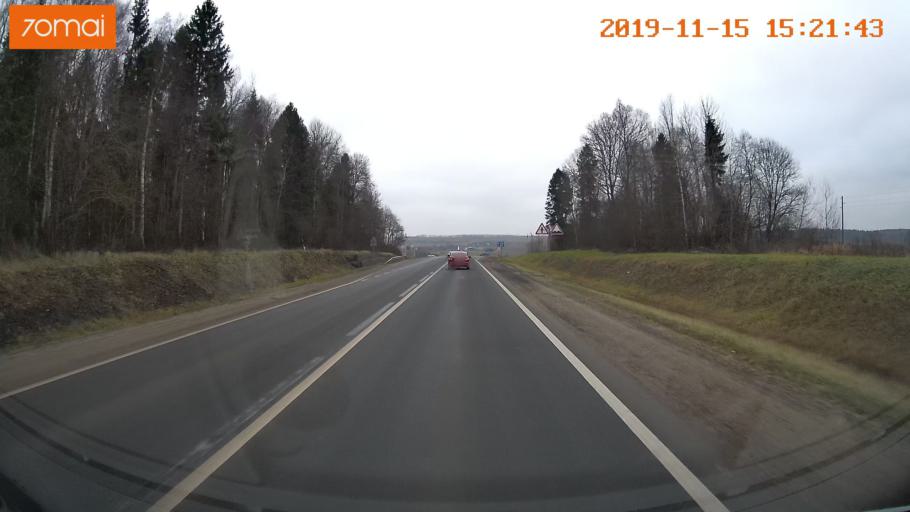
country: RU
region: Jaroslavl
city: Danilov
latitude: 58.2097
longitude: 40.1414
